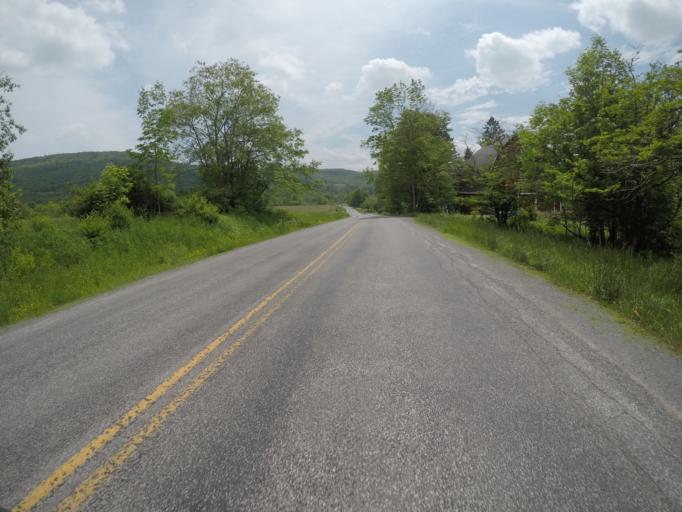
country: US
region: New York
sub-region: Delaware County
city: Stamford
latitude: 42.1972
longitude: -74.6768
